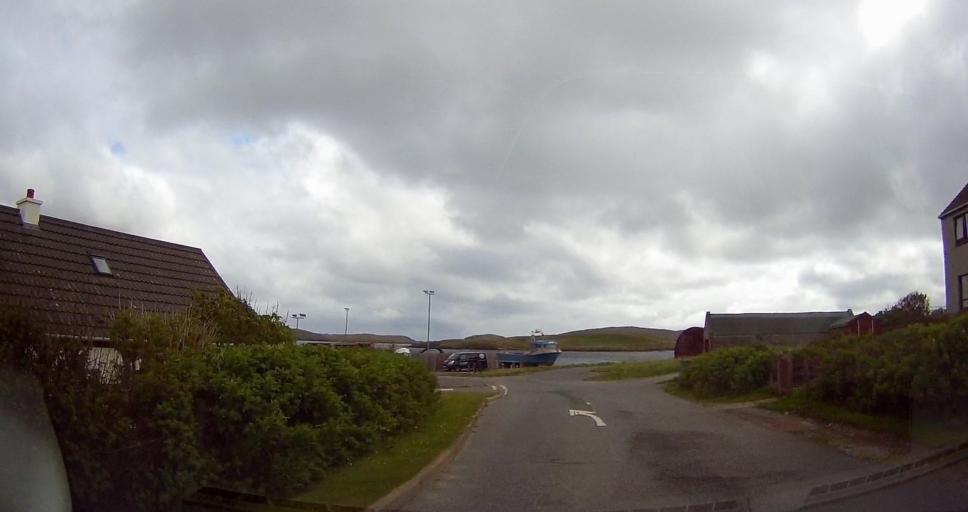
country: GB
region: Scotland
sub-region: Shetland Islands
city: Sandwick
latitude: 60.2243
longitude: -1.5701
